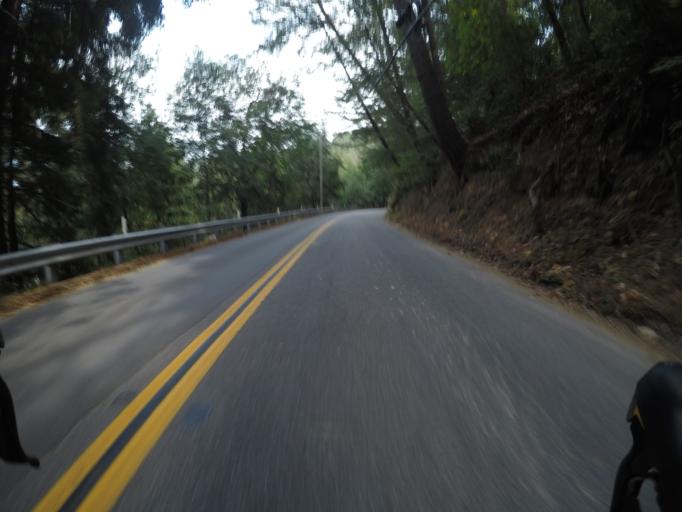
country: US
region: California
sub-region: Santa Cruz County
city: Scotts Valley
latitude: 37.0836
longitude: -122.0072
